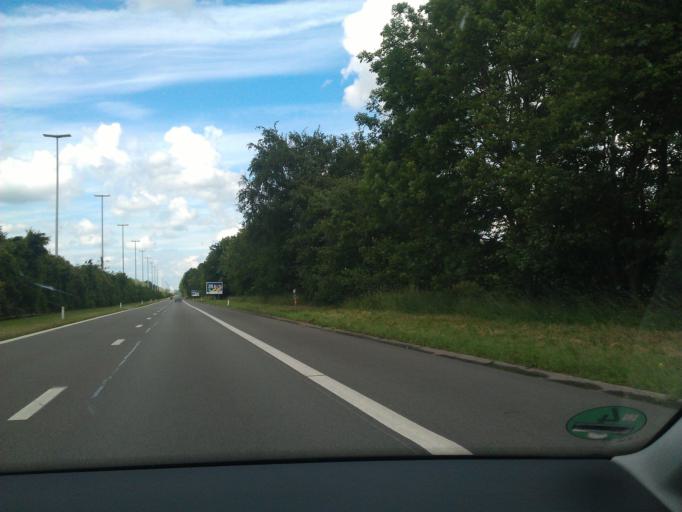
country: BE
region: Wallonia
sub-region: Province de Liege
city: Lontzen
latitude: 50.6602
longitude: 6.0187
